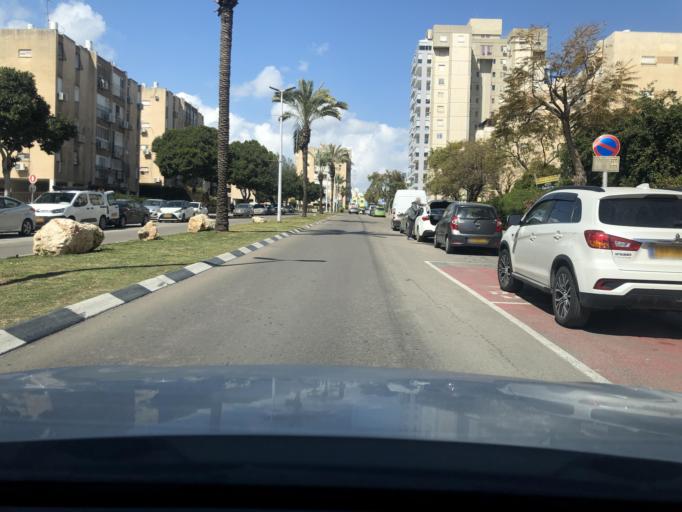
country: IL
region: Tel Aviv
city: Bat Yam
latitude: 32.0078
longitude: 34.7547
